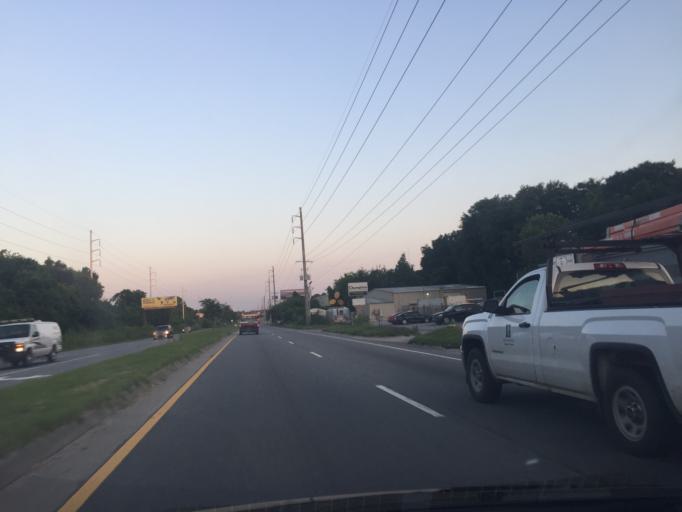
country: US
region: Georgia
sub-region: Chatham County
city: Thunderbolt
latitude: 32.0709
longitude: -81.0614
